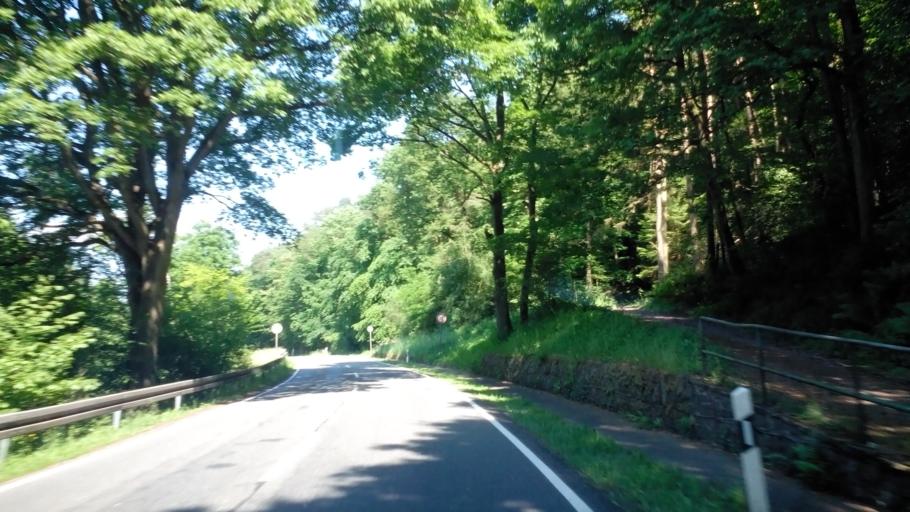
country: DE
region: Saarland
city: Saarwellingen
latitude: 49.3764
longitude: 6.8043
